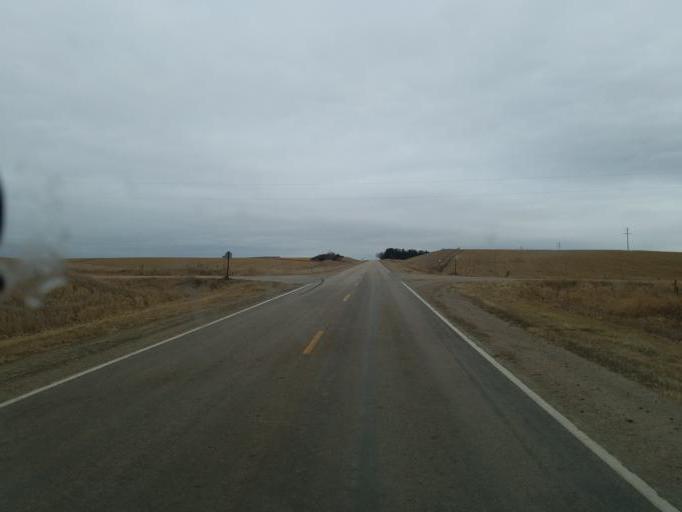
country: US
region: Nebraska
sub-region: Knox County
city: Bloomfield
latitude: 42.5979
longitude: -97.6041
